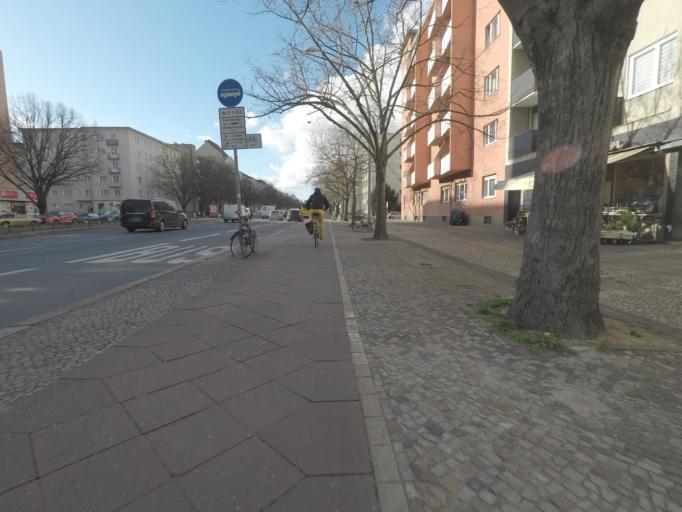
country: DE
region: Berlin
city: Charlottenburg-Nord
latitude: 52.5151
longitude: 13.3145
